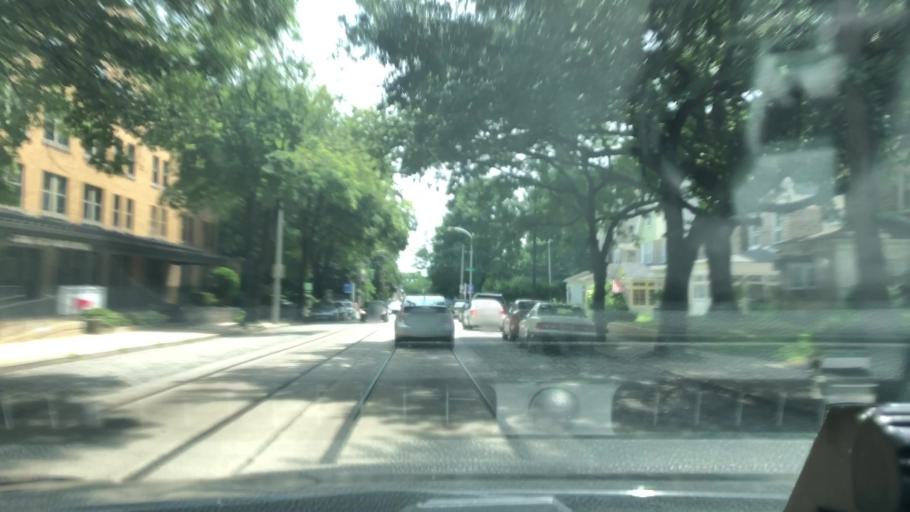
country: US
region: Pennsylvania
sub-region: Montgomery County
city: Wyndmoor
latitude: 40.0481
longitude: -75.1833
